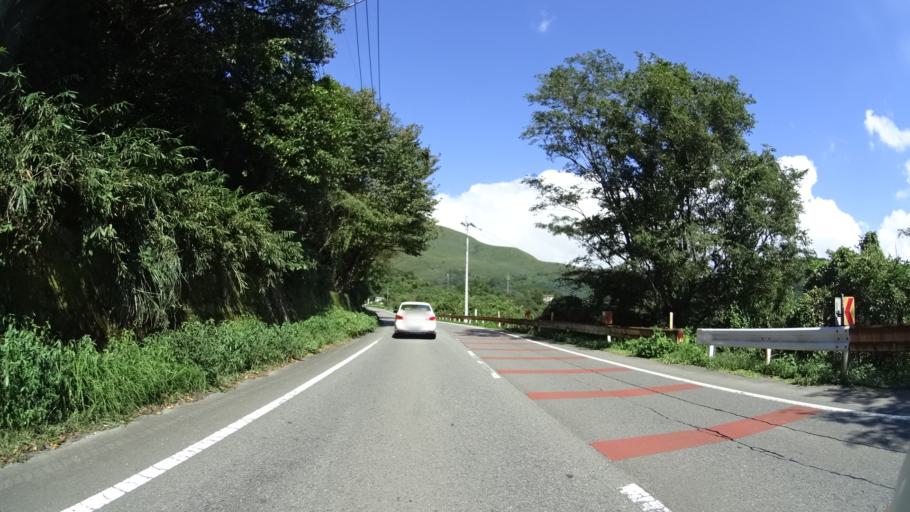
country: JP
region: Oita
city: Beppu
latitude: 33.3216
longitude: 131.4563
